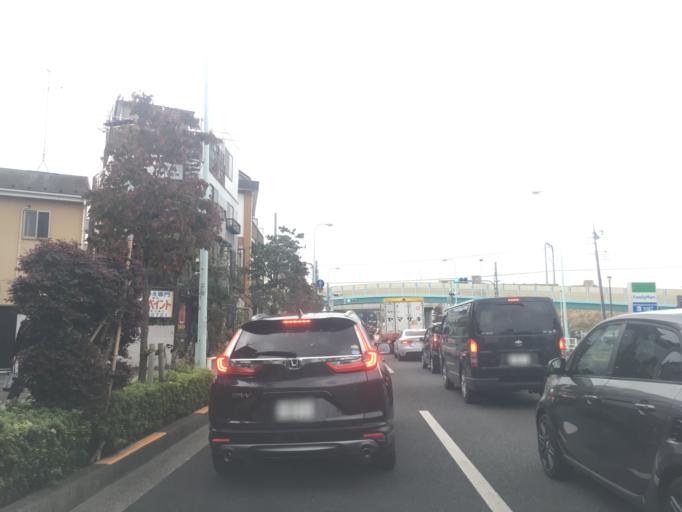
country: JP
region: Tokyo
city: Higashimurayama-shi
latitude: 35.7463
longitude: 139.4669
